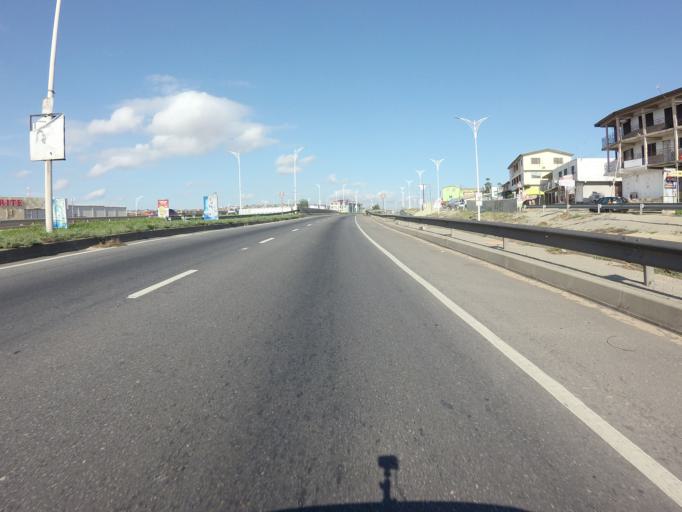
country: GH
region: Greater Accra
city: Gbawe
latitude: 5.5463
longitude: -0.3437
